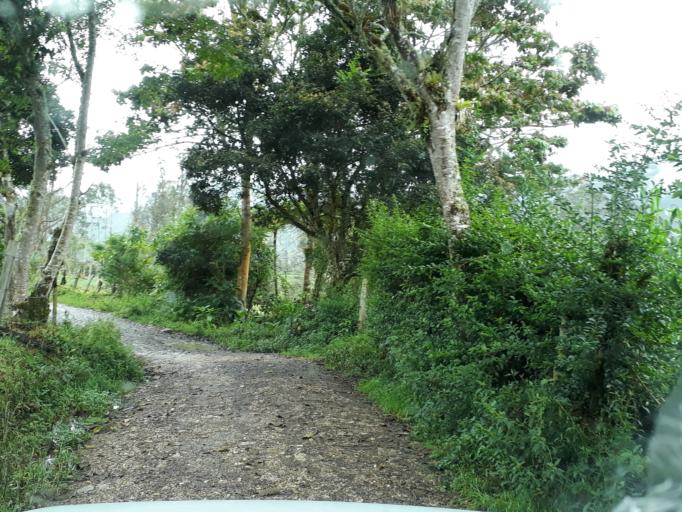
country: CO
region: Cundinamarca
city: Gacheta
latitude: 4.8713
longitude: -73.6317
